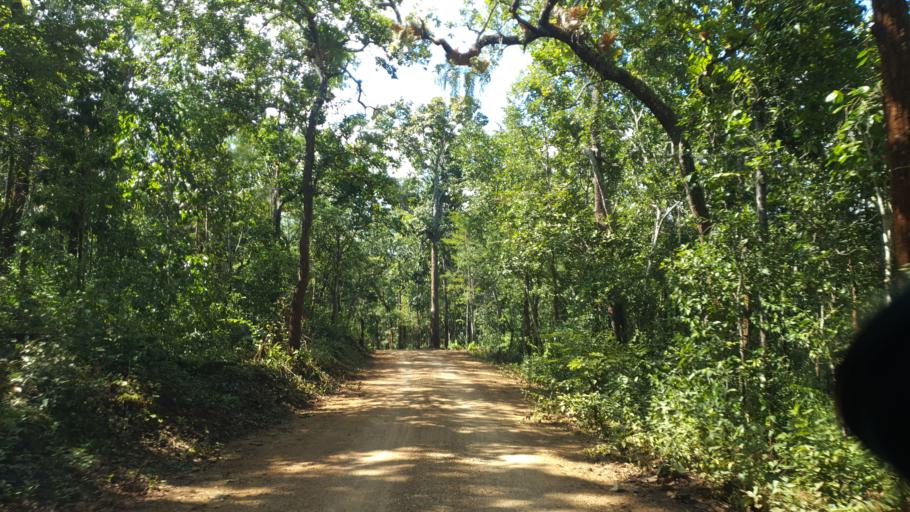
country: TH
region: Chiang Mai
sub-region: Amphoe Chiang Dao
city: Chiang Dao
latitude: 19.3027
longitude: 98.7236
